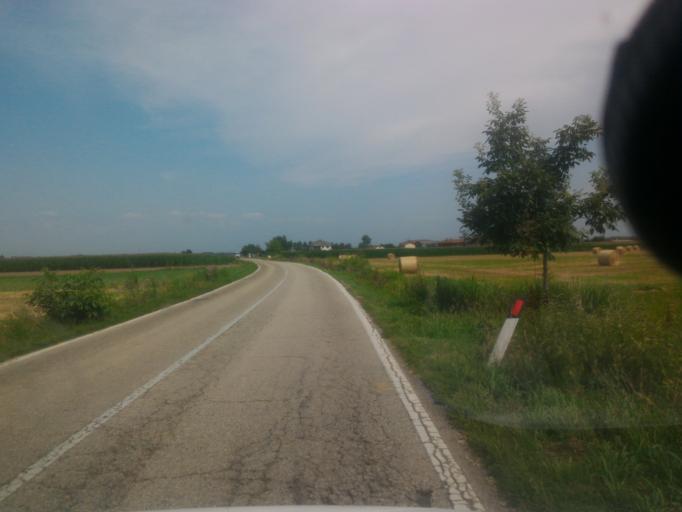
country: IT
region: Piedmont
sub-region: Provincia di Torino
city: Buriasco
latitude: 44.8588
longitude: 7.4310
